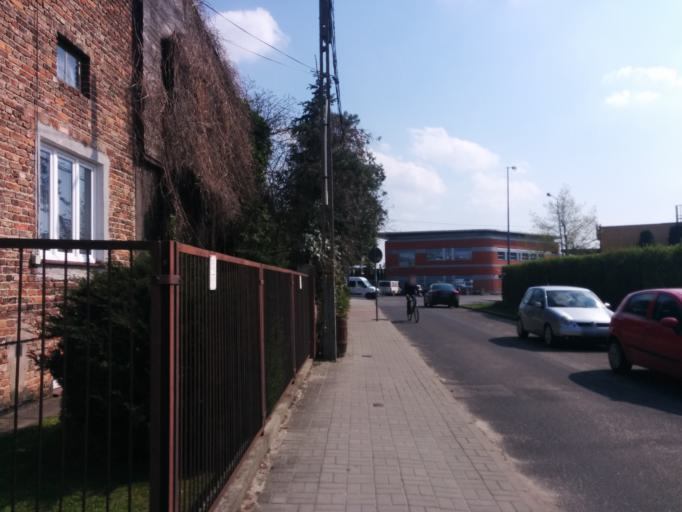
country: PL
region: Masovian Voivodeship
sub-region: Warszawa
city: Wlochy
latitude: 52.1951
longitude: 20.9531
